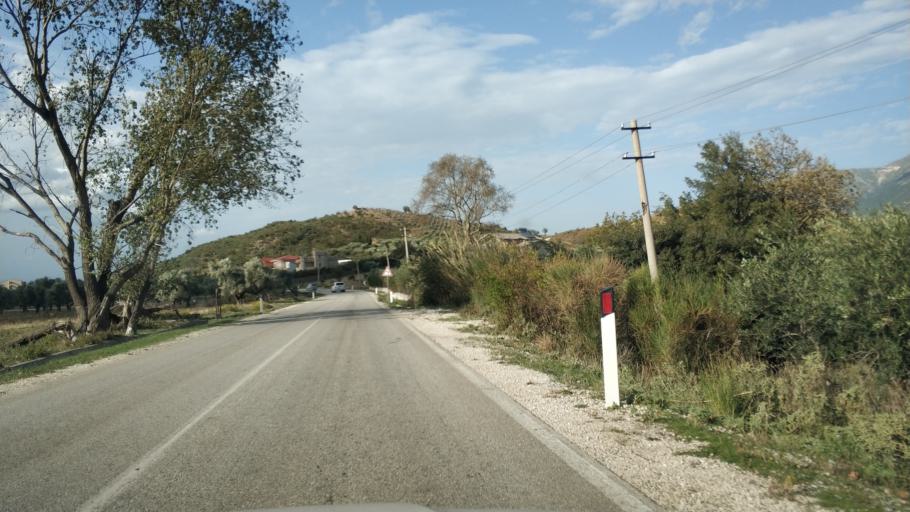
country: AL
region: Vlore
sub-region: Rrethi i Vlores
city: Orikum
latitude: 40.2944
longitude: 19.4906
